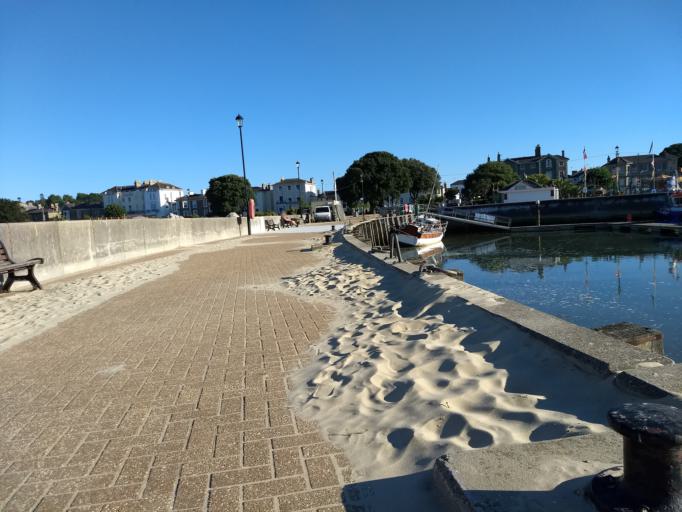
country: GB
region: England
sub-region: Isle of Wight
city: Ryde
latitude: 50.7323
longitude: -1.1533
